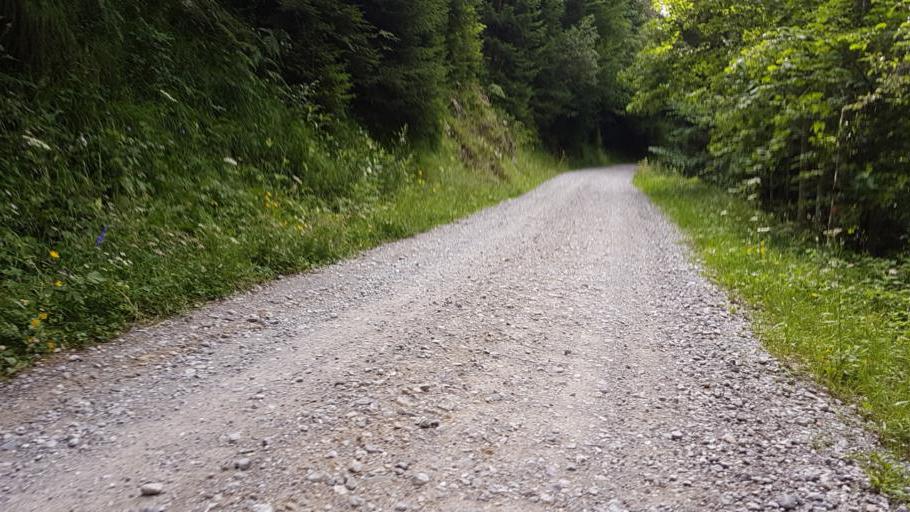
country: CH
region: Bern
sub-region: Obersimmental-Saanen District
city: Boltigen
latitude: 46.6789
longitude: 7.4516
